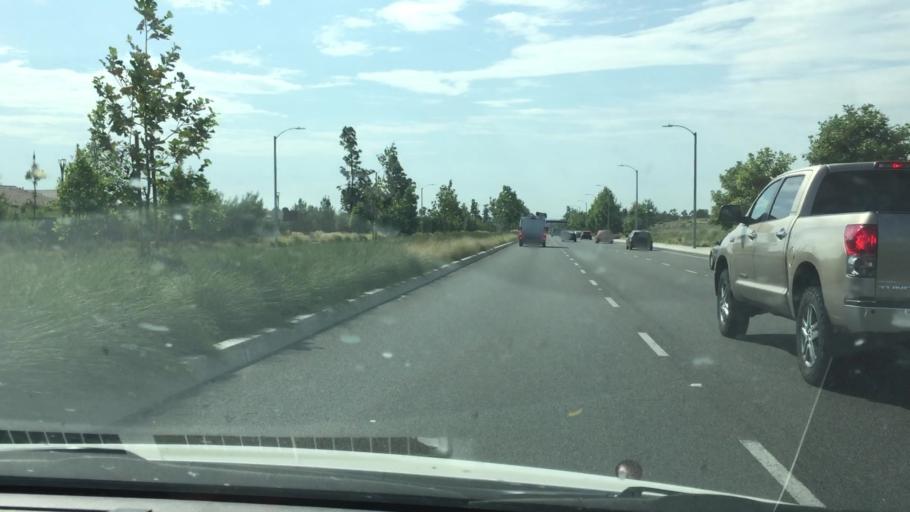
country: US
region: California
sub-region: Orange County
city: Lake Forest
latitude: 33.6904
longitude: -117.7264
